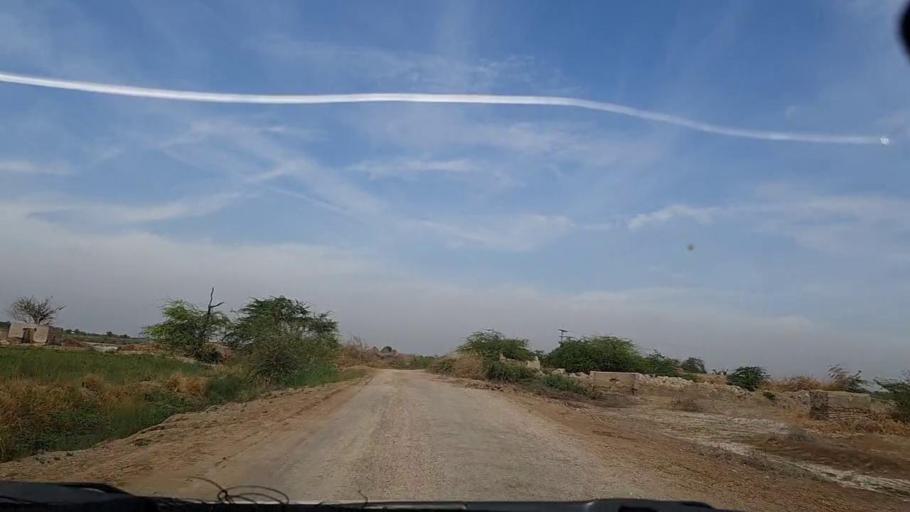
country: PK
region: Sindh
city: Pithoro
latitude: 25.4743
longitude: 69.4574
